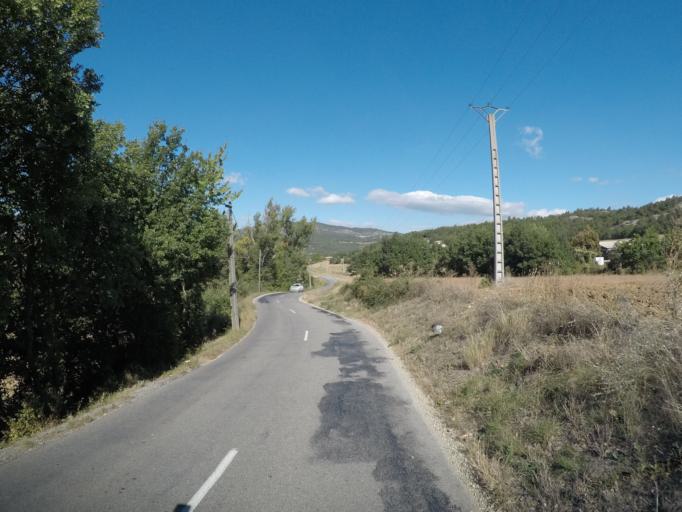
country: FR
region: Provence-Alpes-Cote d'Azur
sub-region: Departement des Alpes-de-Haute-Provence
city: Mallemoisson
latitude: 44.0428
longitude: 6.1681
